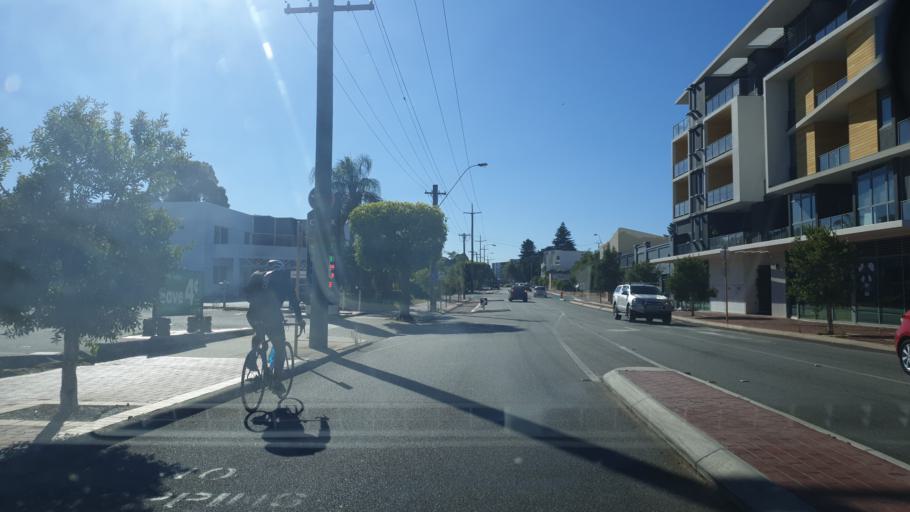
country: AU
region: Western Australia
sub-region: Vincent
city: Mount Lawley
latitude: -31.9427
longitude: 115.8673
